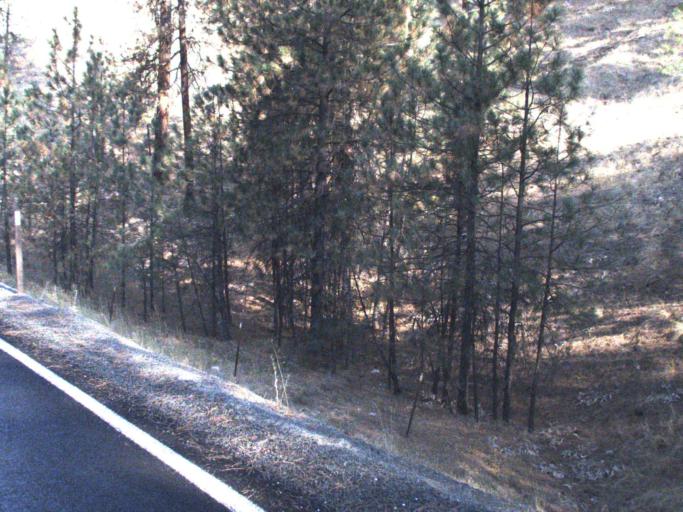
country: US
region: Washington
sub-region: Spokane County
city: Deer Park
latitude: 47.8752
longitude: -117.6516
